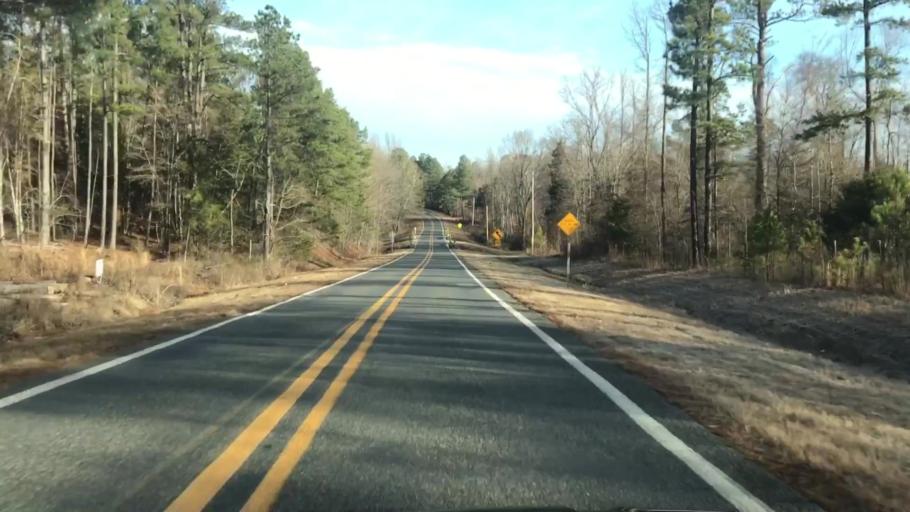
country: US
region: Arkansas
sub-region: Garland County
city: Rockwell
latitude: 34.4897
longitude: -93.2761
